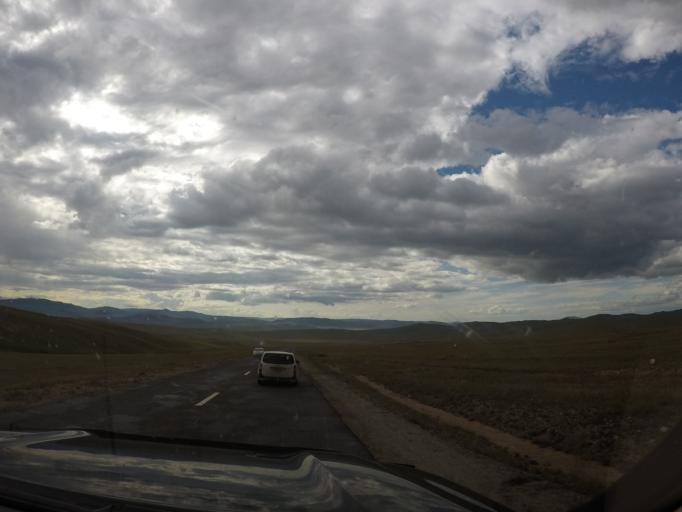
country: MN
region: Hentiy
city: Modot
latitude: 47.5888
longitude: 109.2820
